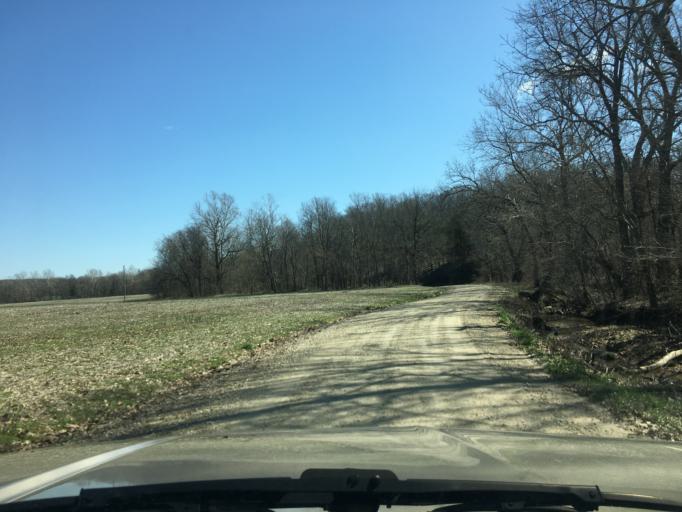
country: US
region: Missouri
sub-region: Franklin County
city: New Haven
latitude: 38.5533
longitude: -91.3263
